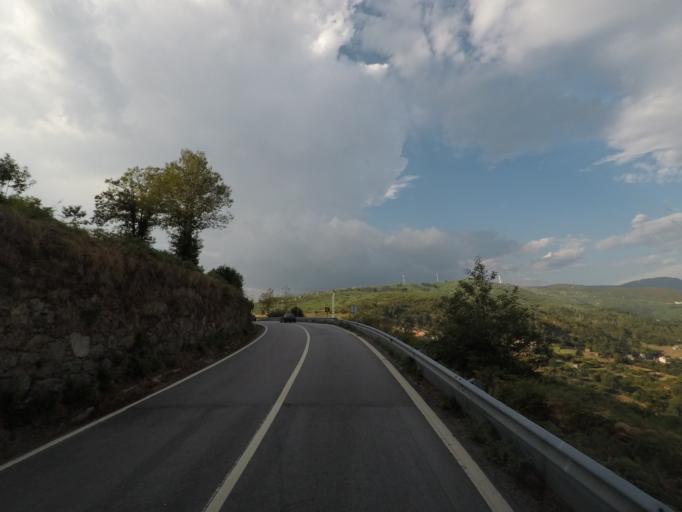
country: PT
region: Porto
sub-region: Baiao
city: Valadares
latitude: 41.1913
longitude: -7.9455
